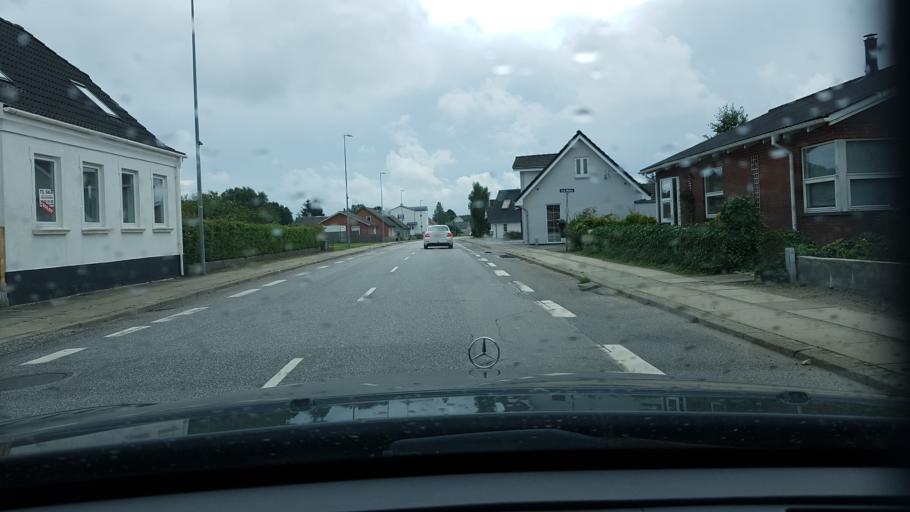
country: DK
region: North Denmark
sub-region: Mariagerfjord Kommune
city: Hadsund
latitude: 56.8024
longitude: 10.2721
